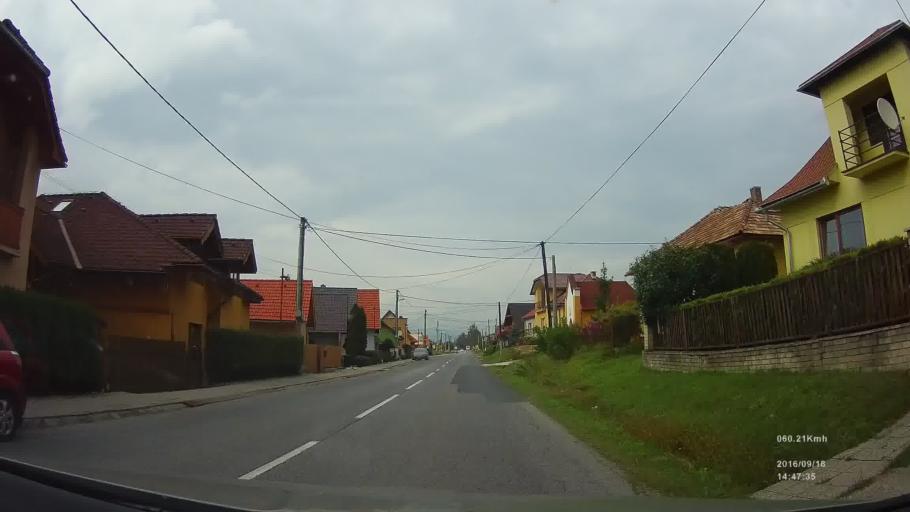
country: SK
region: Kosicky
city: Spisska Nova Ves
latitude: 48.9674
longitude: 20.5827
